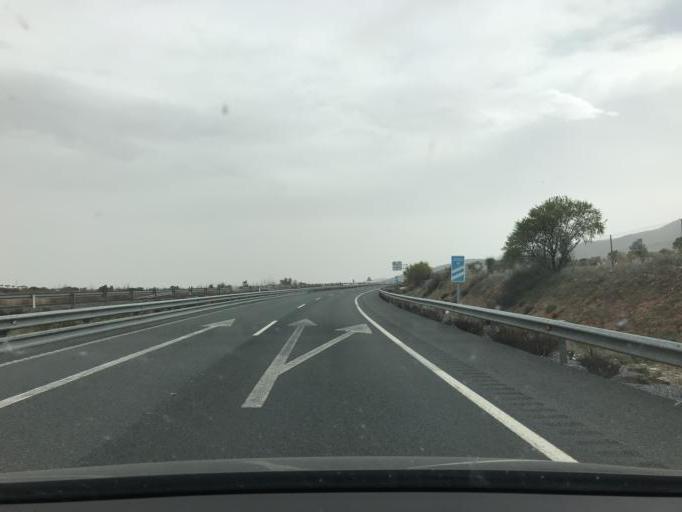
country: ES
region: Andalusia
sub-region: Provincia de Granada
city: Gor
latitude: 37.3958
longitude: -2.9561
